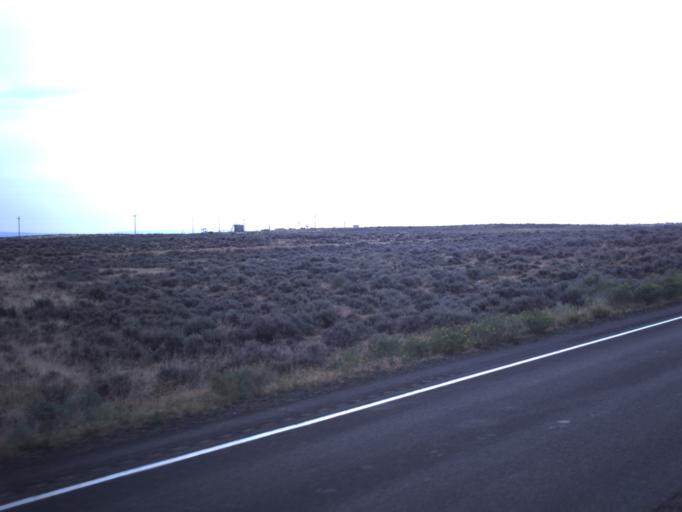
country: US
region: Utah
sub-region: Uintah County
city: Naples
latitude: 40.2011
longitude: -109.3495
